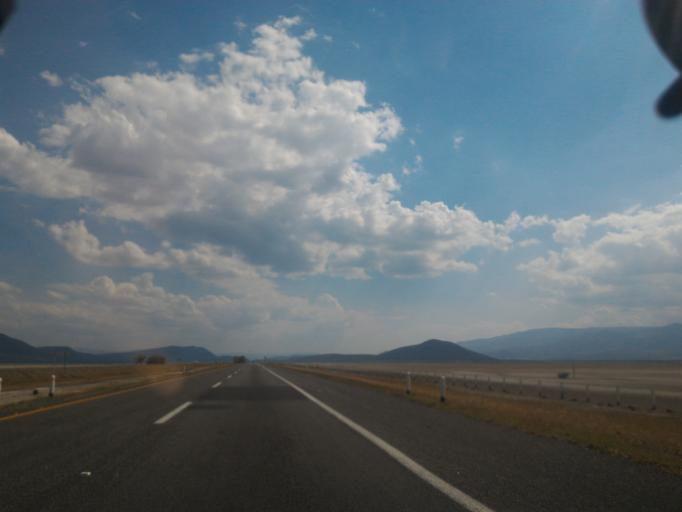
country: MX
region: Jalisco
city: Zacoalco de Torres
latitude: 20.3146
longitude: -103.5634
